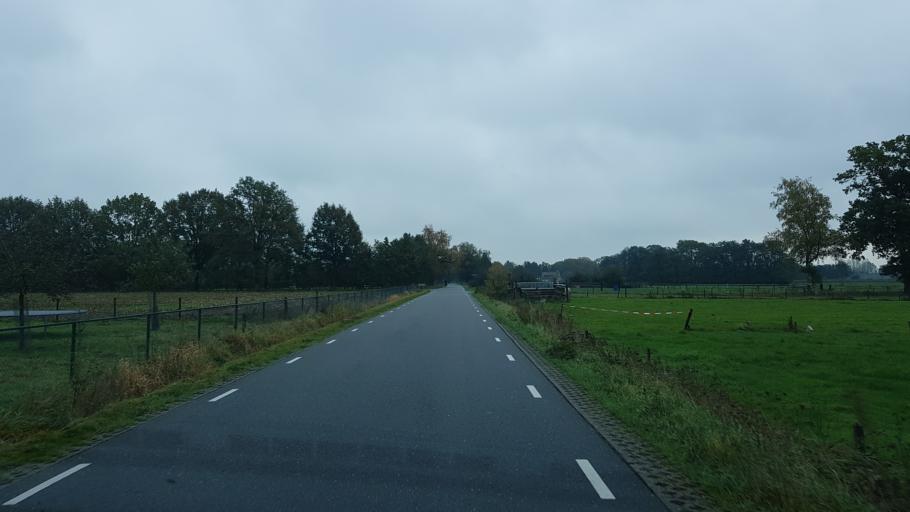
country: NL
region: Gelderland
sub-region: Gemeente Epe
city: Vaassen
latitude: 52.2555
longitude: 5.9744
